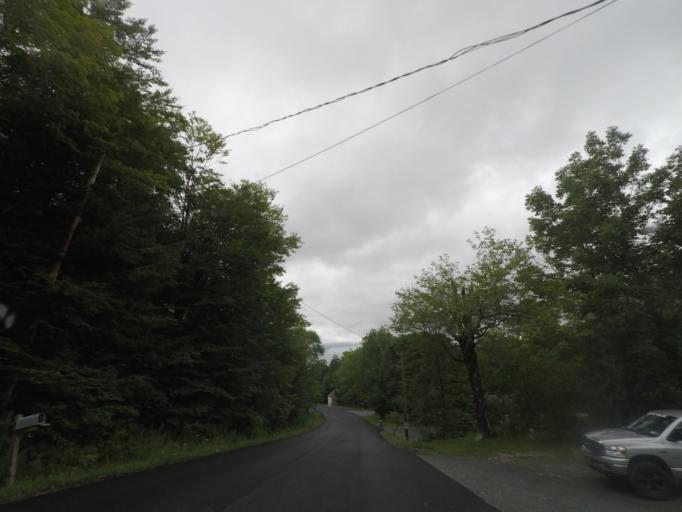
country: US
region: New York
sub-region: Rensselaer County
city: Poestenkill
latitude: 42.6898
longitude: -73.4847
